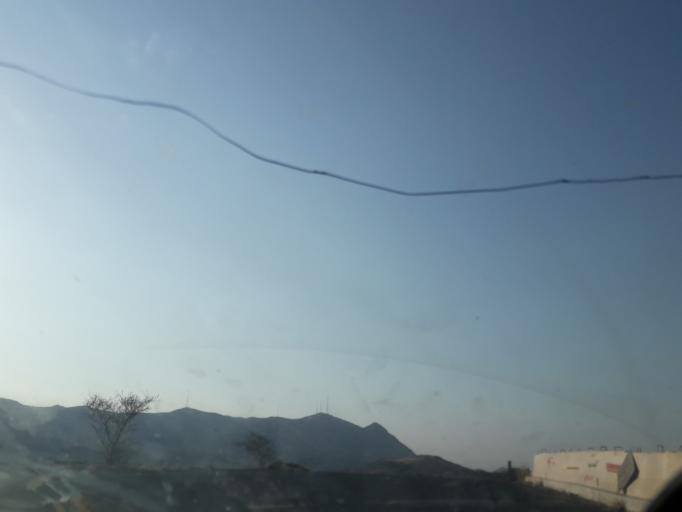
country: SA
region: Makkah
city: Ta'if
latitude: 21.2714
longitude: 40.3746
